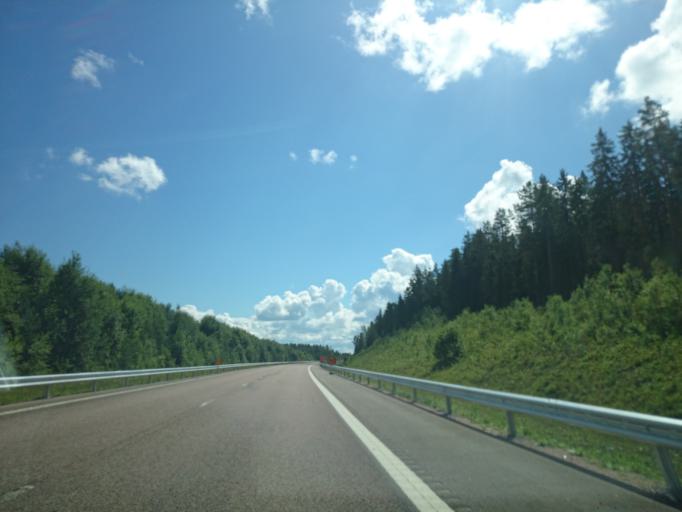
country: SE
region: Gaevleborg
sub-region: Gavle Kommun
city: Gavle
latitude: 60.5568
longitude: 17.2512
